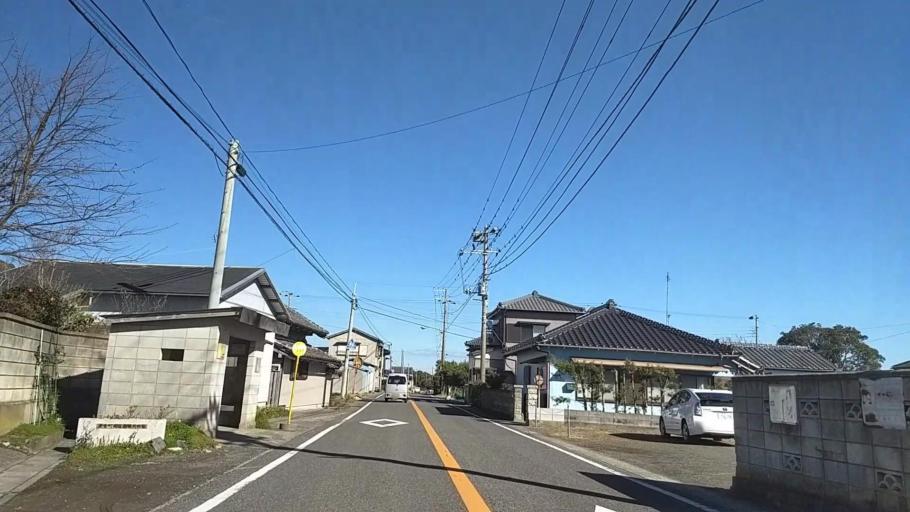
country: JP
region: Chiba
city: Tateyama
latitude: 34.9335
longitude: 139.9486
